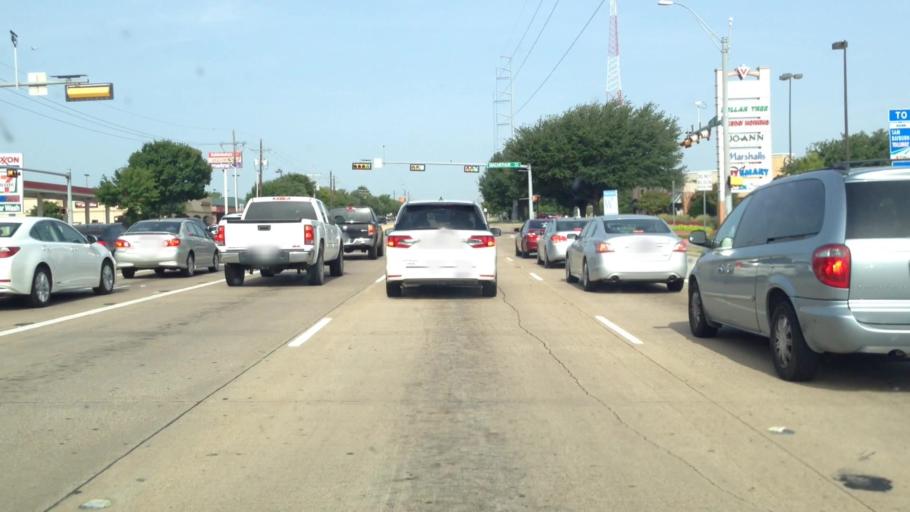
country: US
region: Texas
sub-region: Denton County
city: Lewisville
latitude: 33.0048
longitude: -96.9777
